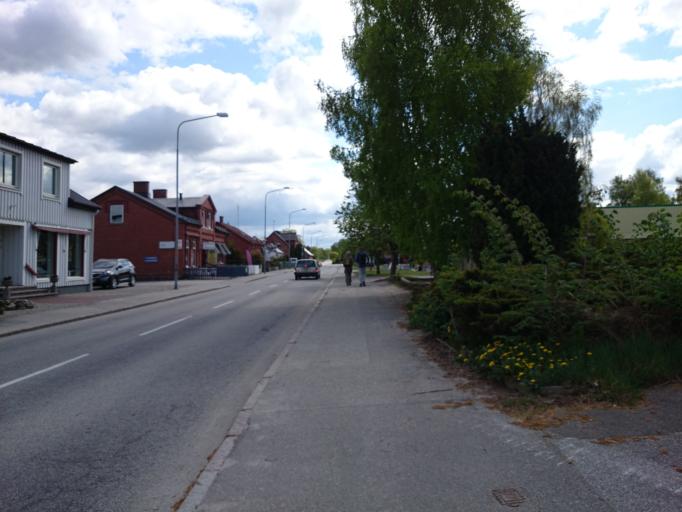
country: SE
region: Skane
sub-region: Lunds Kommun
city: Genarp
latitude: 55.5991
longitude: 13.4024
